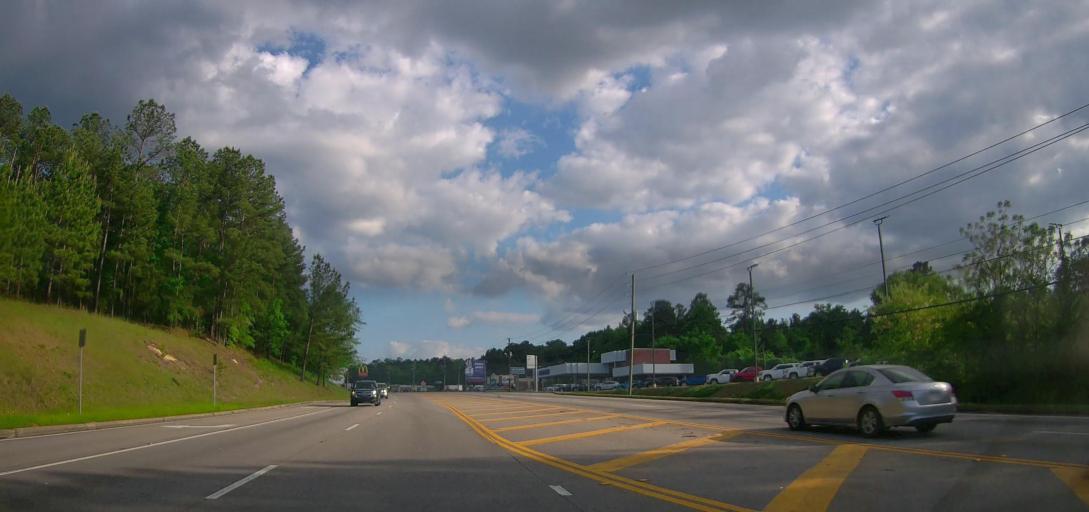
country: US
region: Georgia
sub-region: Baldwin County
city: Milledgeville
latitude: 33.1162
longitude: -83.2604
